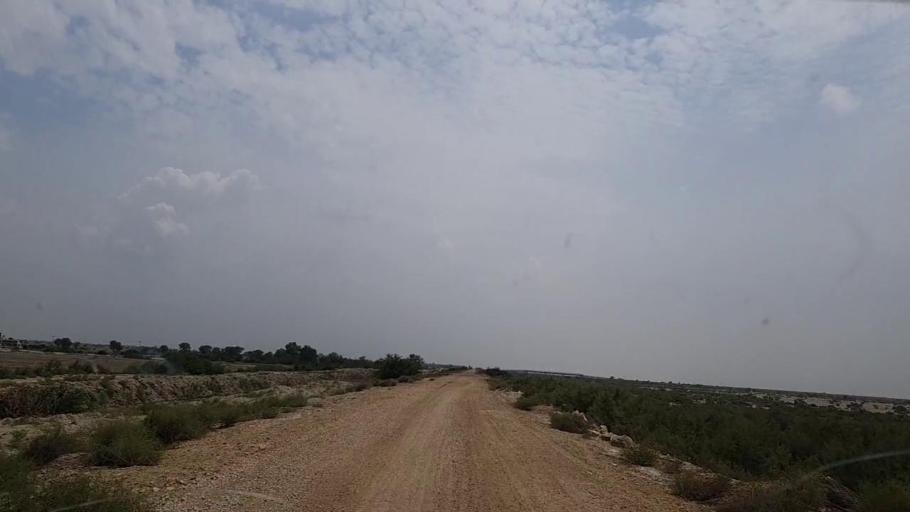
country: PK
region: Sindh
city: Phulji
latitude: 26.8292
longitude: 67.6165
